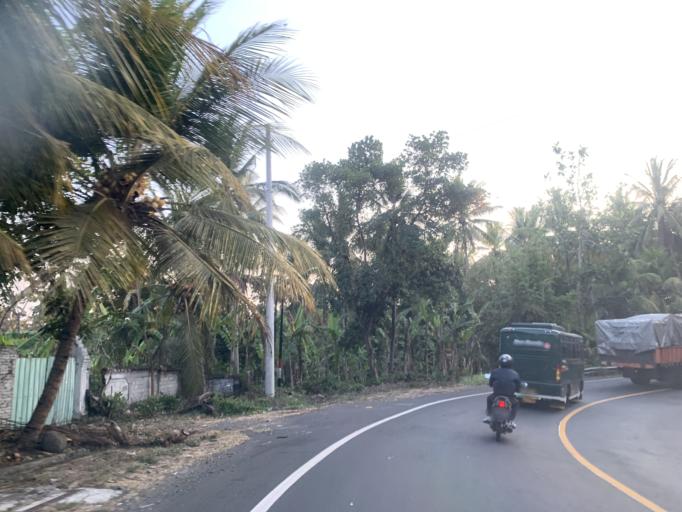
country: ID
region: Bali
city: Banjar Swastika
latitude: -8.4334
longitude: 114.8564
